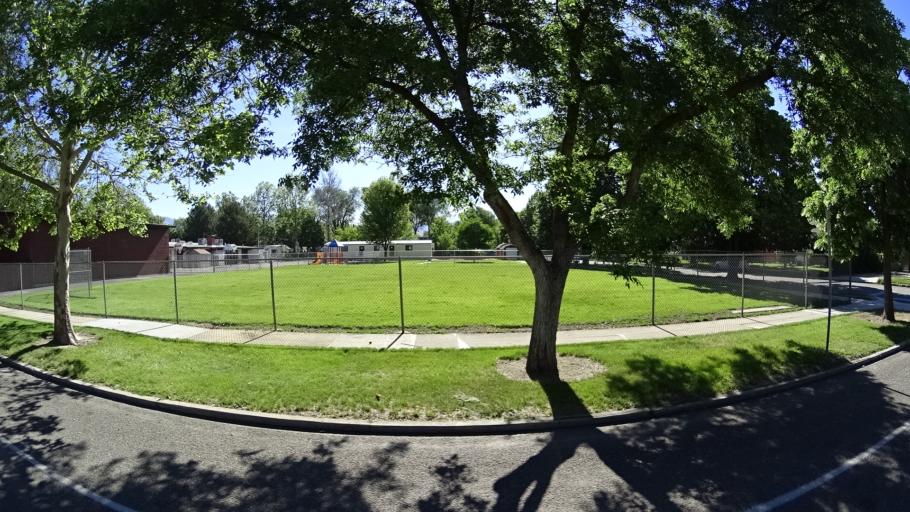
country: US
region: Idaho
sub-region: Ada County
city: Boise
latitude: 43.6247
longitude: -116.2184
